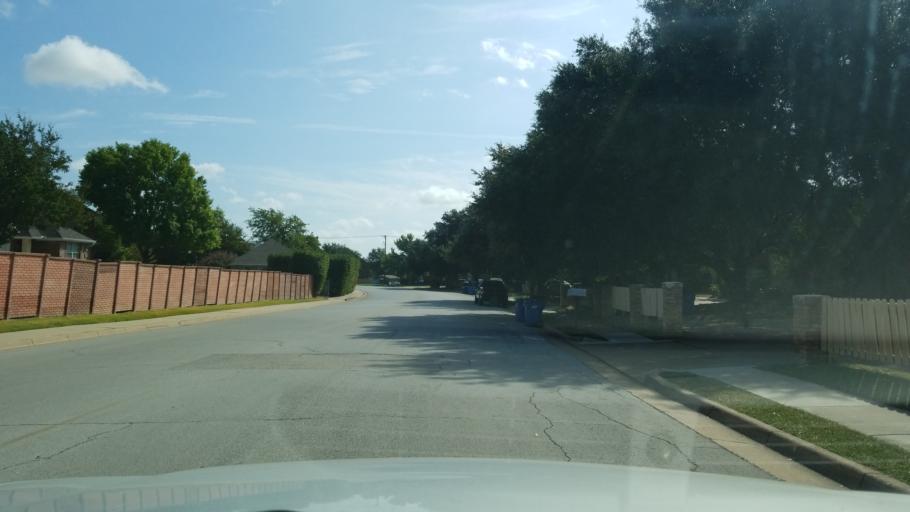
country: US
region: Texas
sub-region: Tarrant County
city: Euless
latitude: 32.8481
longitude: -97.0759
